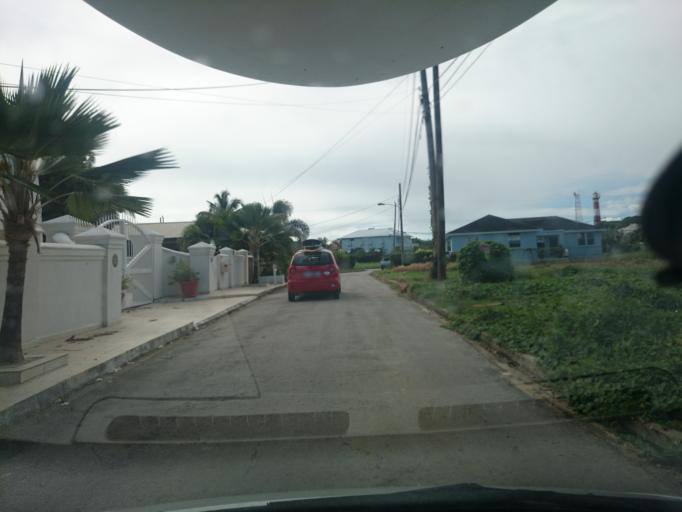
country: BB
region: Christ Church
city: Oistins
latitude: 13.0464
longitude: -59.5256
